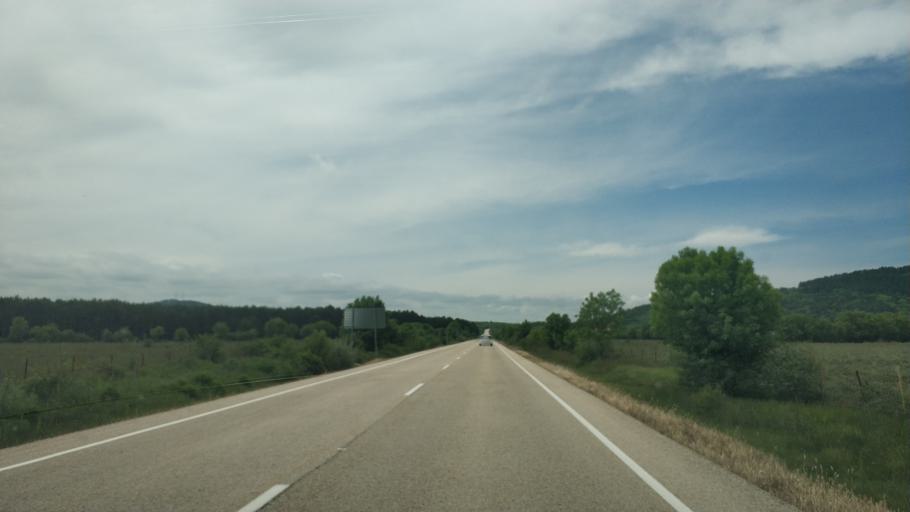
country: ES
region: Castille and Leon
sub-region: Provincia de Soria
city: Sotillo del Rincon
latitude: 41.8945
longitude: -2.6692
